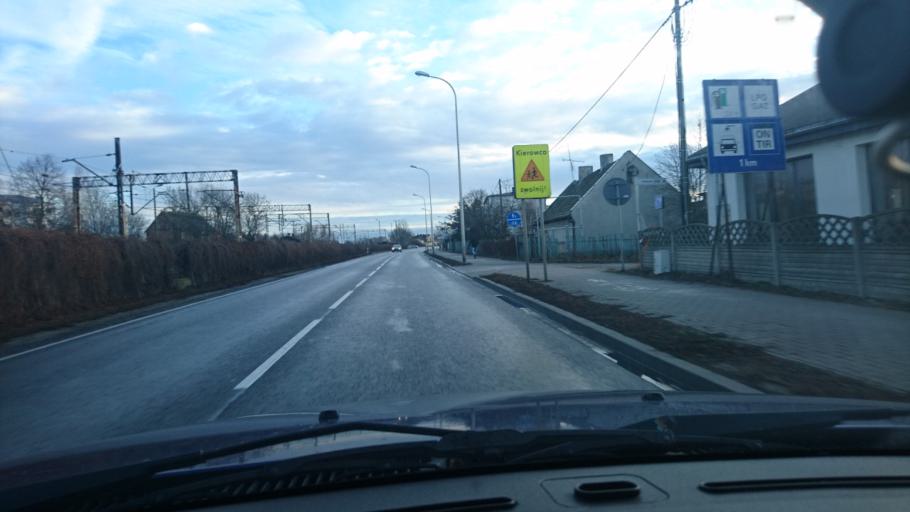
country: PL
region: Greater Poland Voivodeship
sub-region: Powiat kepinski
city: Kepno
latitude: 51.2998
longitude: 17.9960
